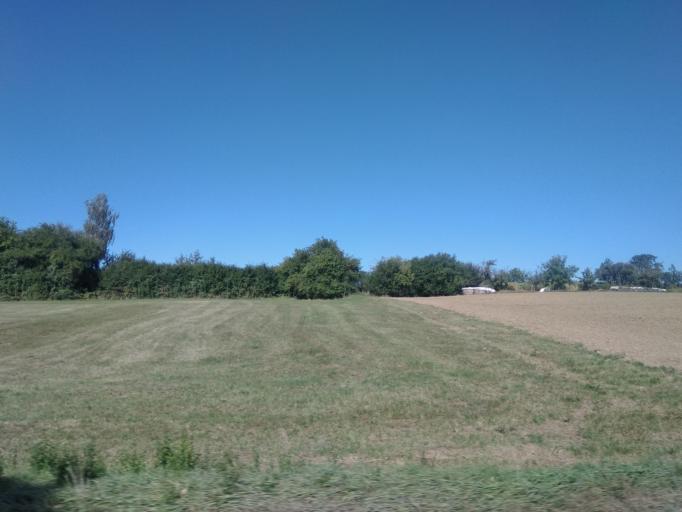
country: DE
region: Baden-Wuerttemberg
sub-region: Karlsruhe Region
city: Billigheim
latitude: 49.4075
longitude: 9.2788
